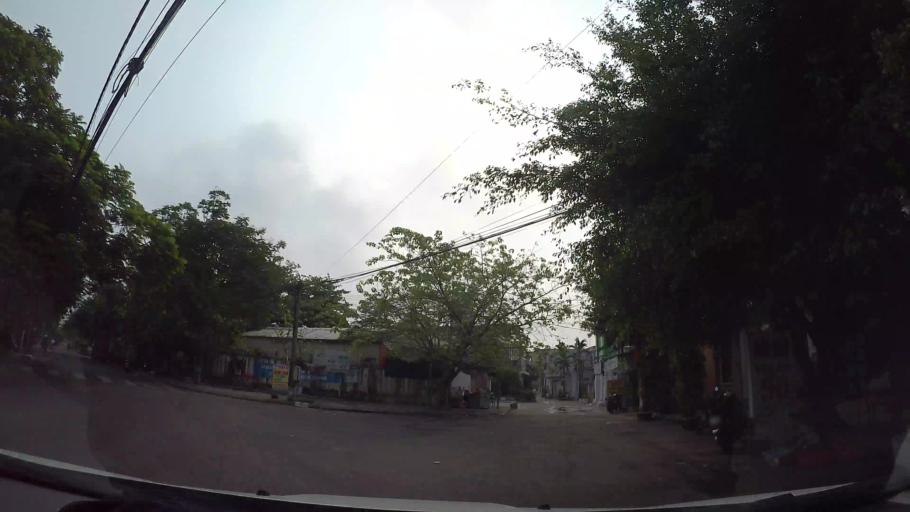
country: VN
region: Da Nang
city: Son Tra
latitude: 16.0927
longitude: 108.2489
